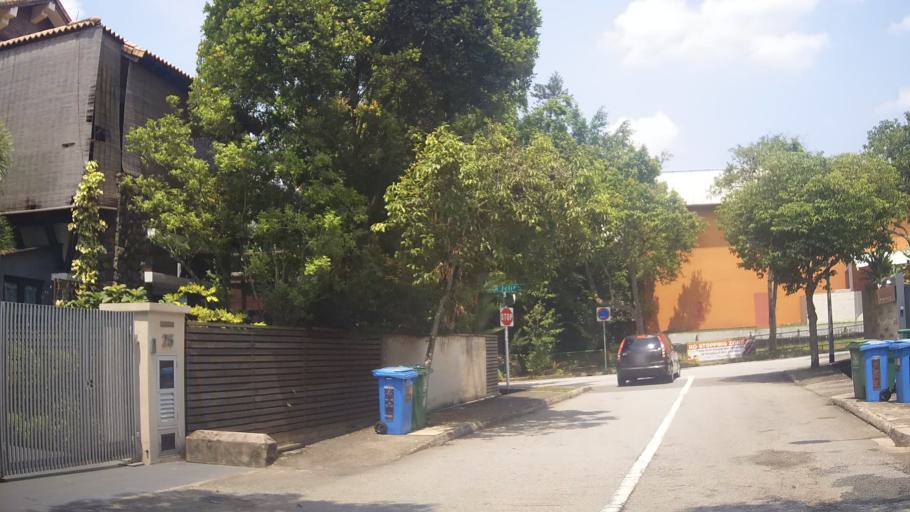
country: SG
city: Singapore
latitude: 1.3173
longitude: 103.7865
